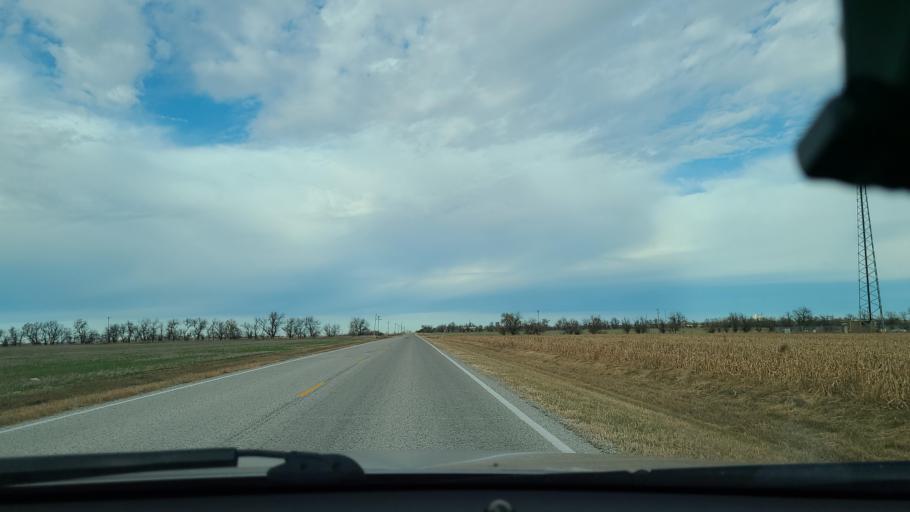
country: US
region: Kansas
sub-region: McPherson County
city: Inman
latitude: 38.3601
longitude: -97.9244
